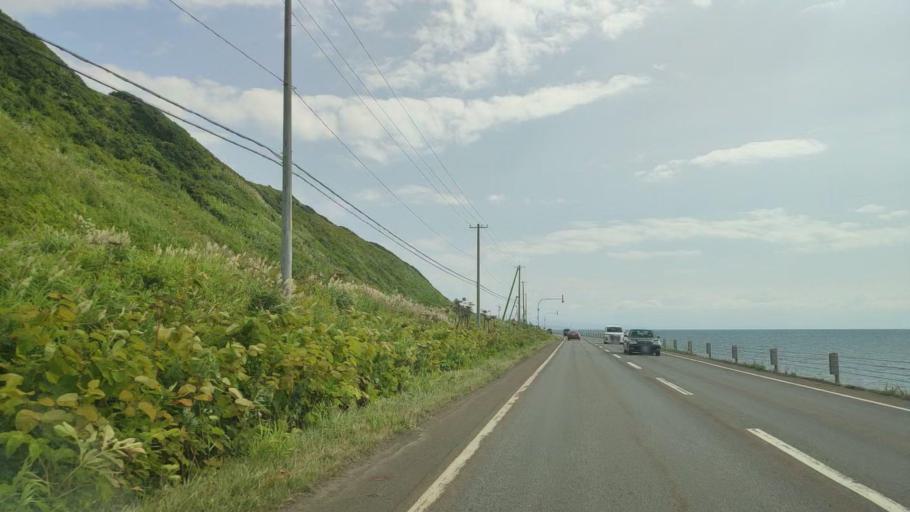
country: JP
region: Hokkaido
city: Rumoi
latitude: 44.0994
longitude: 141.6604
